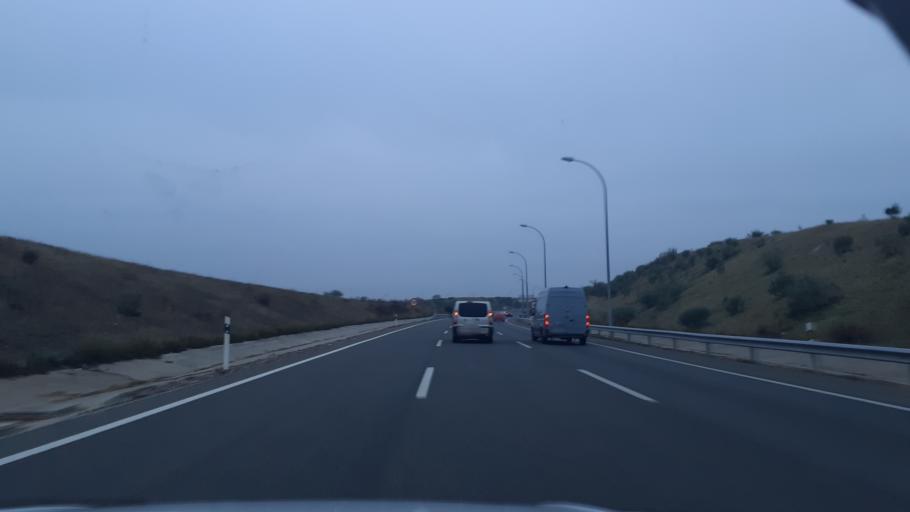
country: ES
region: Madrid
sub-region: Provincia de Madrid
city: Ajalvir
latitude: 40.5054
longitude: -3.4957
